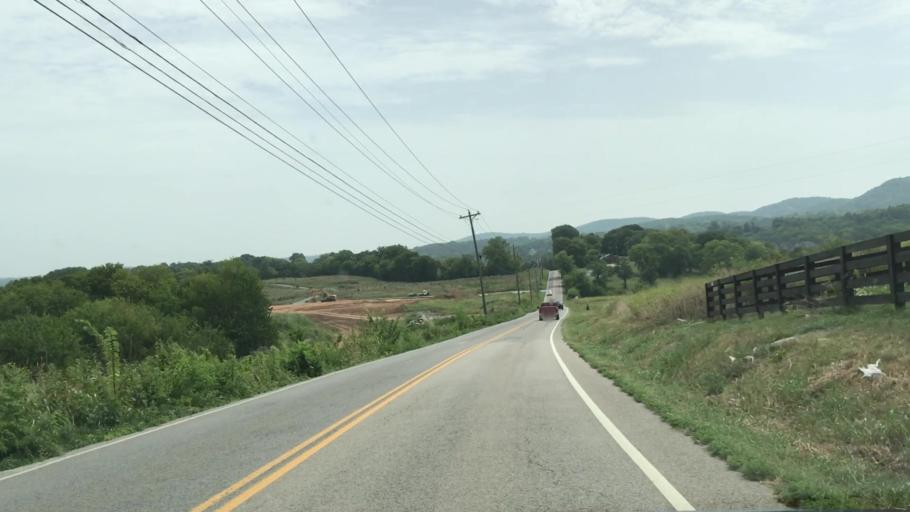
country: US
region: Tennessee
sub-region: Williamson County
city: Nolensville
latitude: 35.9377
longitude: -86.7032
